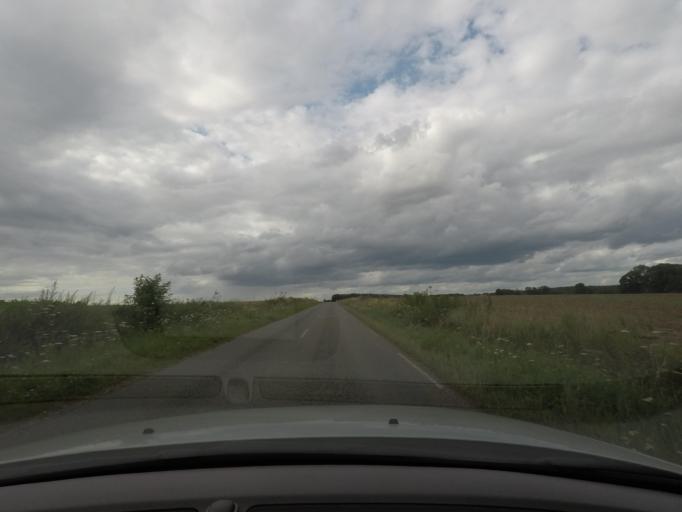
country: FR
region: Haute-Normandie
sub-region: Departement de l'Eure
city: Les Andelys
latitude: 49.2617
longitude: 1.3608
